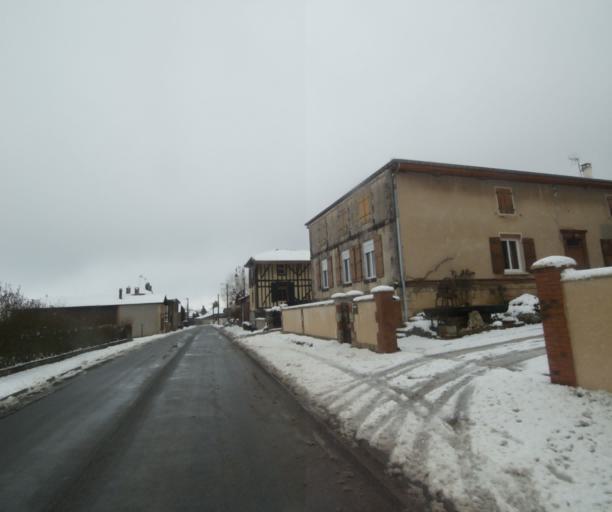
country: FR
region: Champagne-Ardenne
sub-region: Departement de la Haute-Marne
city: Laneuville-a-Remy
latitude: 48.4623
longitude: 4.8450
